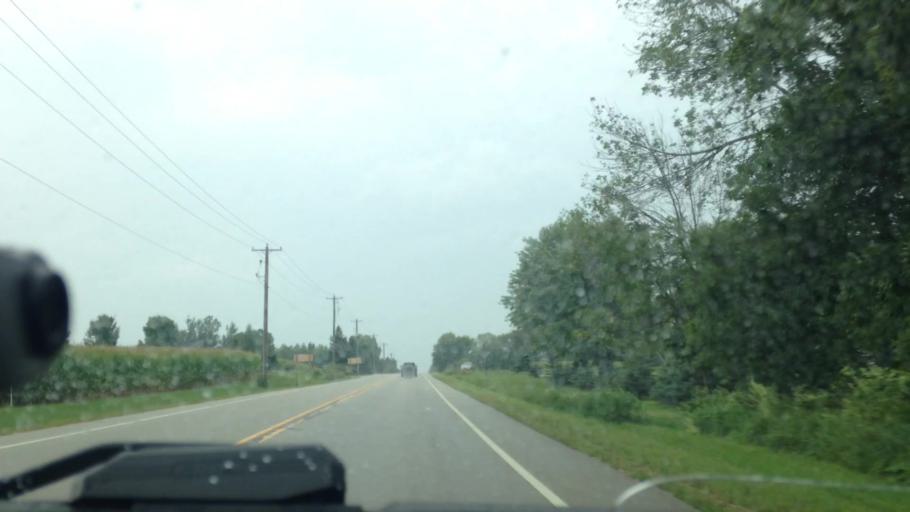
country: US
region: Wisconsin
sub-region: Washington County
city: Hartford
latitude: 43.3986
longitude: -88.3626
